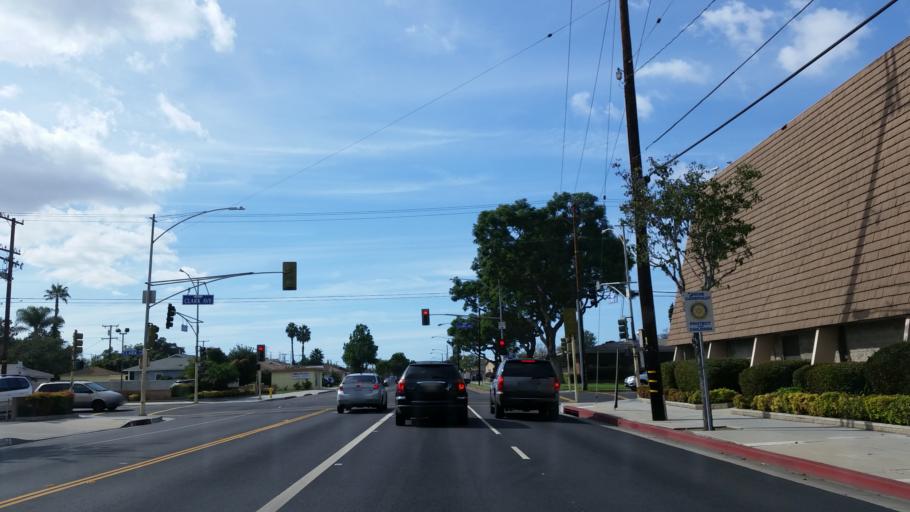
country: US
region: California
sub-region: Los Angeles County
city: Bellflower
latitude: 33.8821
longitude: -118.1334
